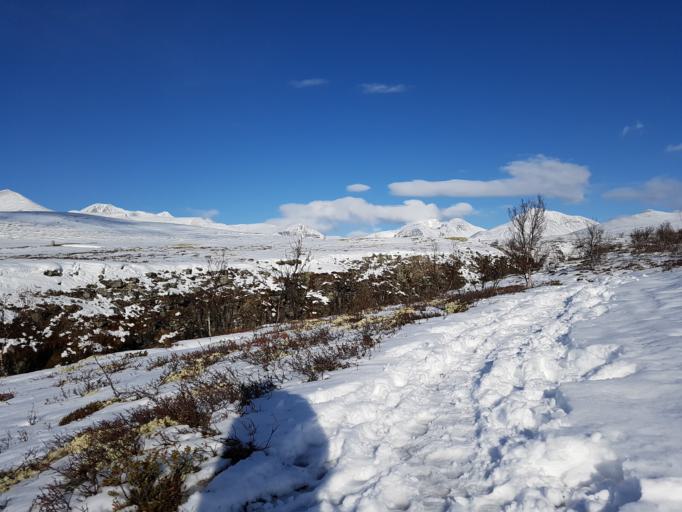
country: NO
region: Oppland
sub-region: Sel
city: Otta
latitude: 61.8307
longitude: 9.7001
